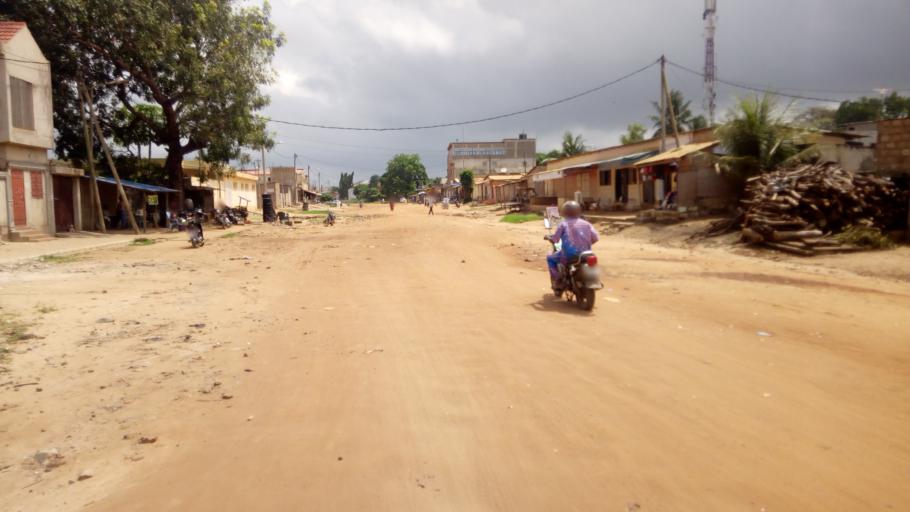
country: TG
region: Maritime
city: Lome
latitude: 6.1924
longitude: 1.1929
